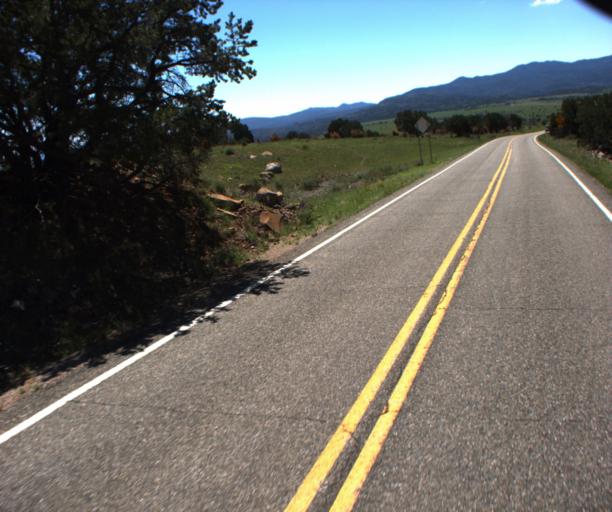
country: US
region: Arizona
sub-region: Greenlee County
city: Morenci
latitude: 33.3415
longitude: -109.3468
